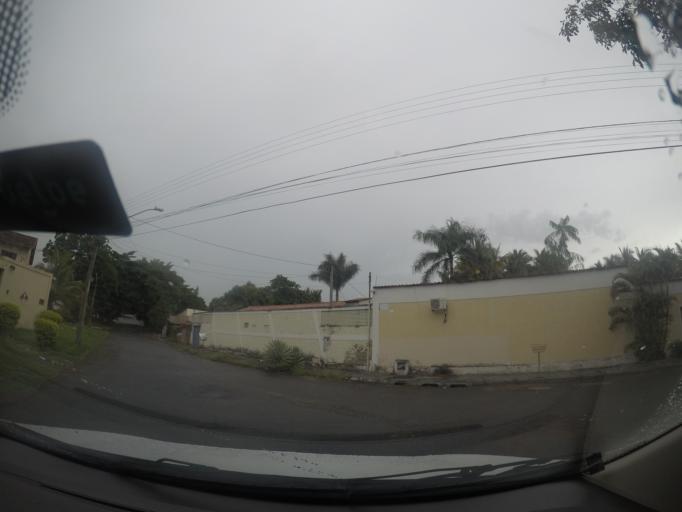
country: BR
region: Goias
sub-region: Goiania
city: Goiania
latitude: -16.6533
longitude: -49.2308
